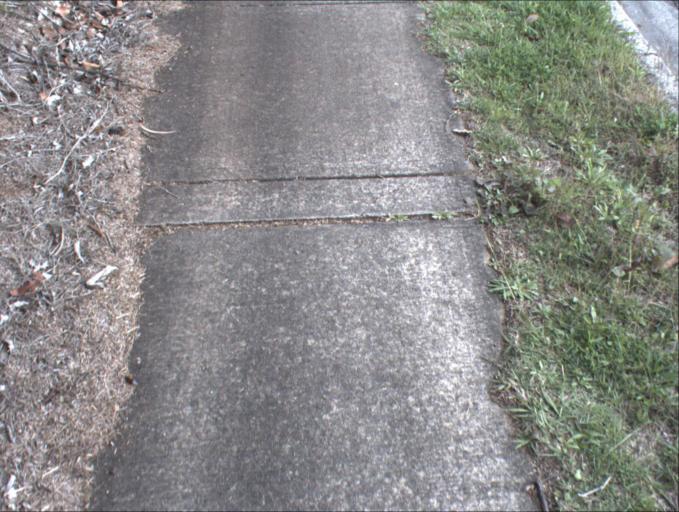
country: AU
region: Queensland
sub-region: Logan
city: Waterford West
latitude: -27.6970
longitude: 153.1557
